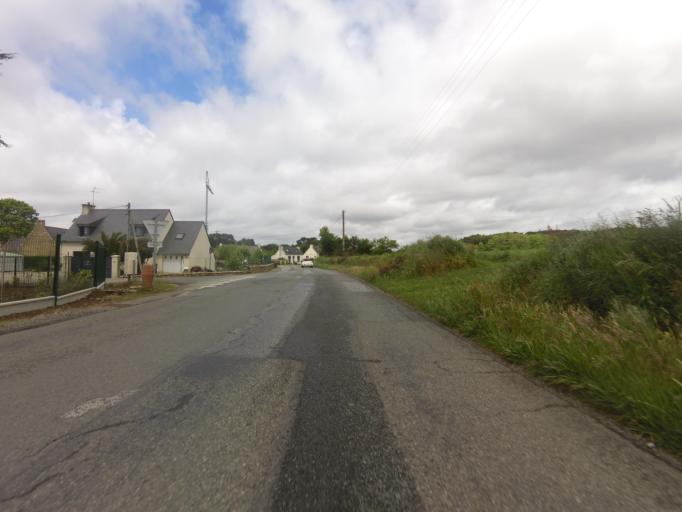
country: FR
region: Brittany
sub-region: Departement du Morbihan
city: Baden
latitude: 47.6033
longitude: -2.9154
